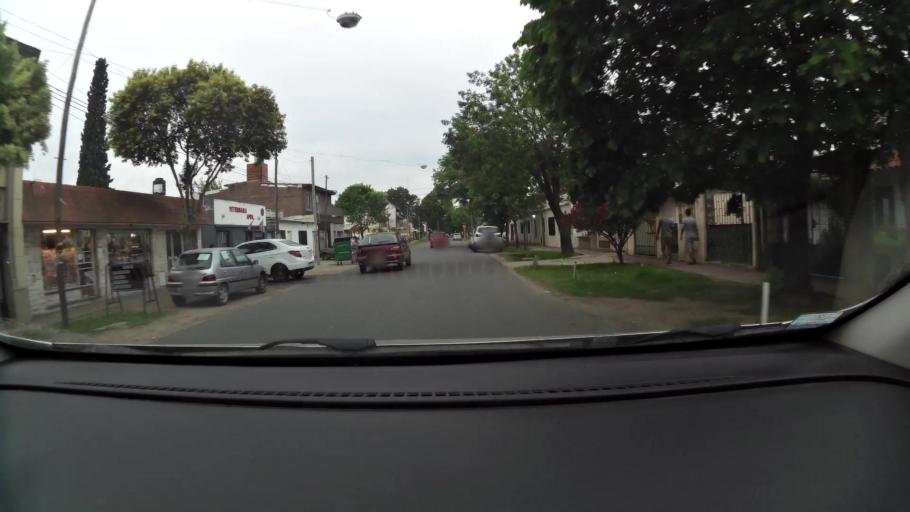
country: AR
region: Santa Fe
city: Granadero Baigorria
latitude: -32.8958
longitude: -60.6998
